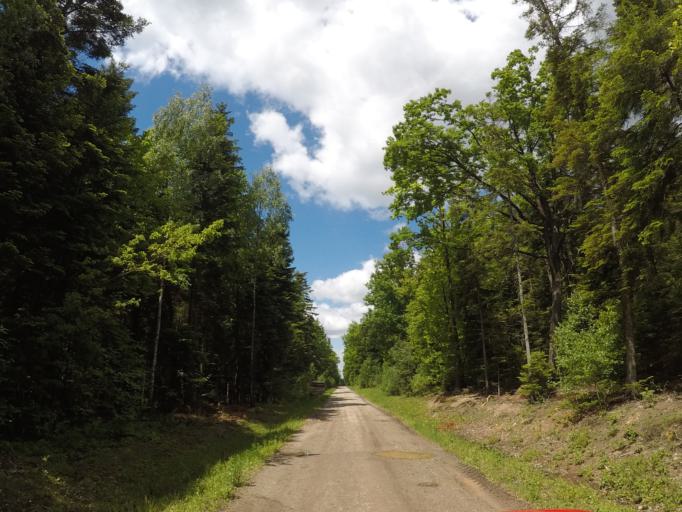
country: PL
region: Swietokrzyskie
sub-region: Powiat kielecki
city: Domaszowice
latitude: 50.9133
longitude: 20.6527
